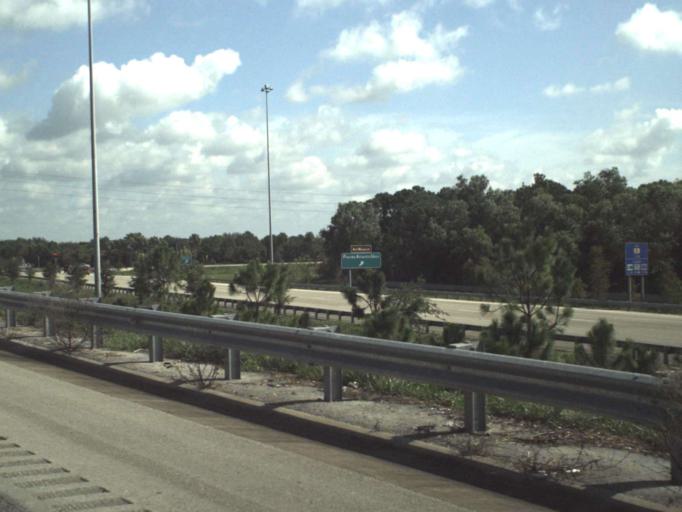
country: US
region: Florida
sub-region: Palm Beach County
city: Palm Beach Gardens
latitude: 26.8805
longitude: -80.1266
